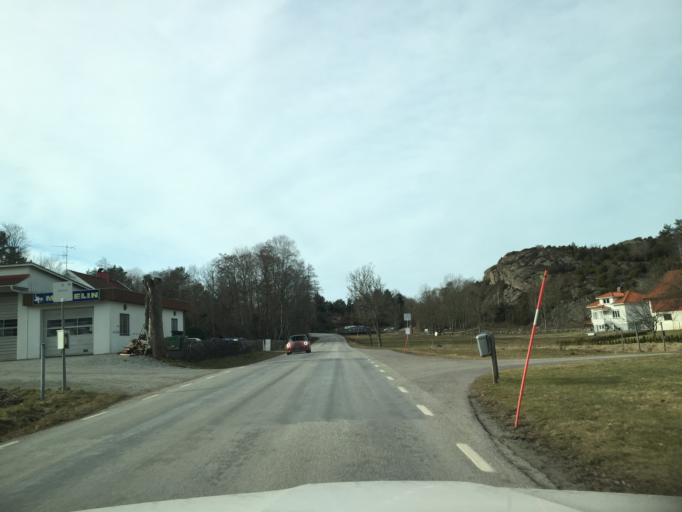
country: SE
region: Vaestra Goetaland
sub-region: Tjorns Kommun
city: Skaerhamn
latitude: 58.0357
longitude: 11.5653
